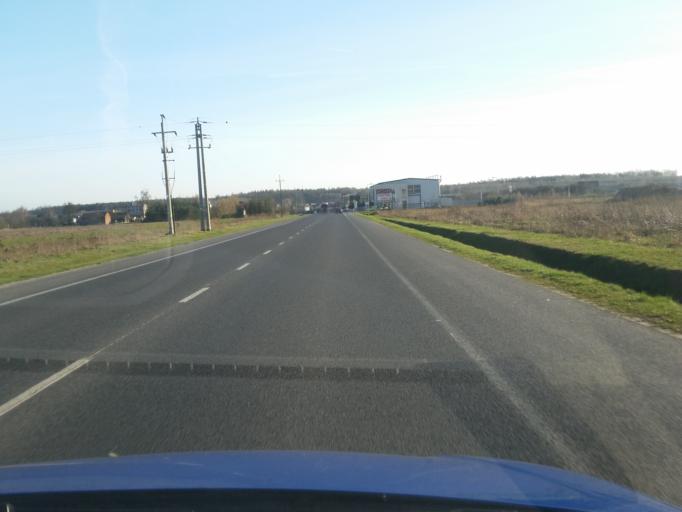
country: PL
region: Lodz Voivodeship
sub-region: Powiat radomszczanski
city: Radomsko
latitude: 51.0830
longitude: 19.3798
